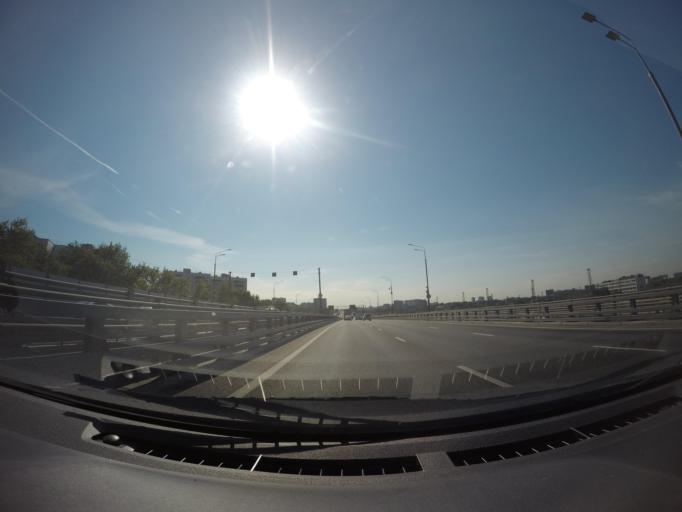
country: RU
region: Moscow
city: Ryazanskiy
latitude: 55.7441
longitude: 37.7516
